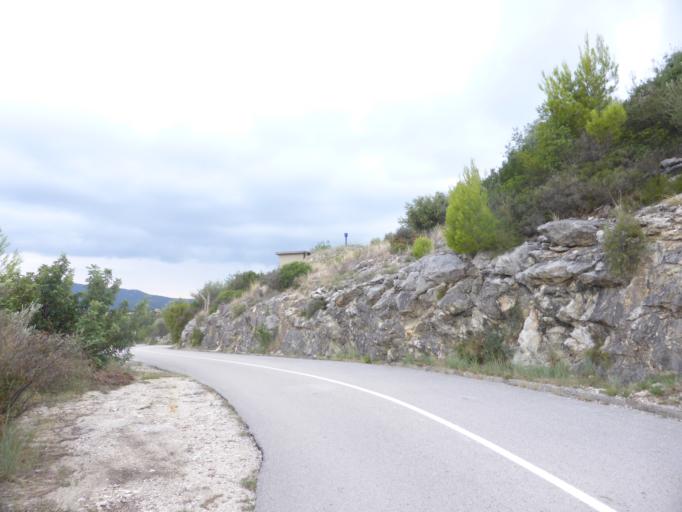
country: HR
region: Dubrovacko-Neretvanska
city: Podgora
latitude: 42.7815
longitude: 17.8690
